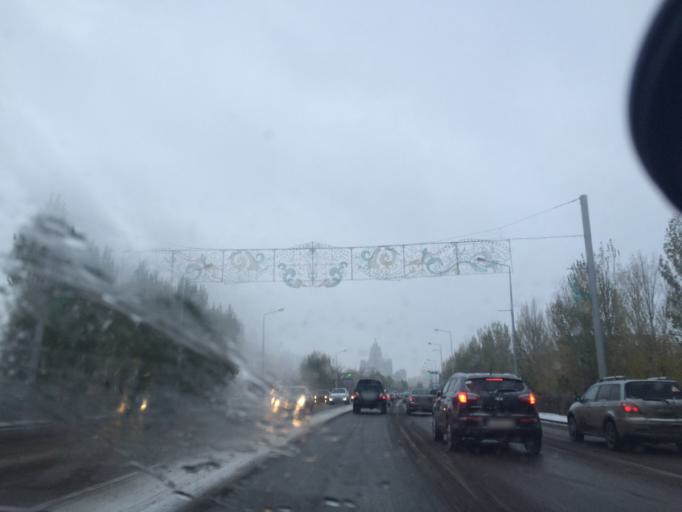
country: KZ
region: Astana Qalasy
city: Astana
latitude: 51.1542
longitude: 71.4123
